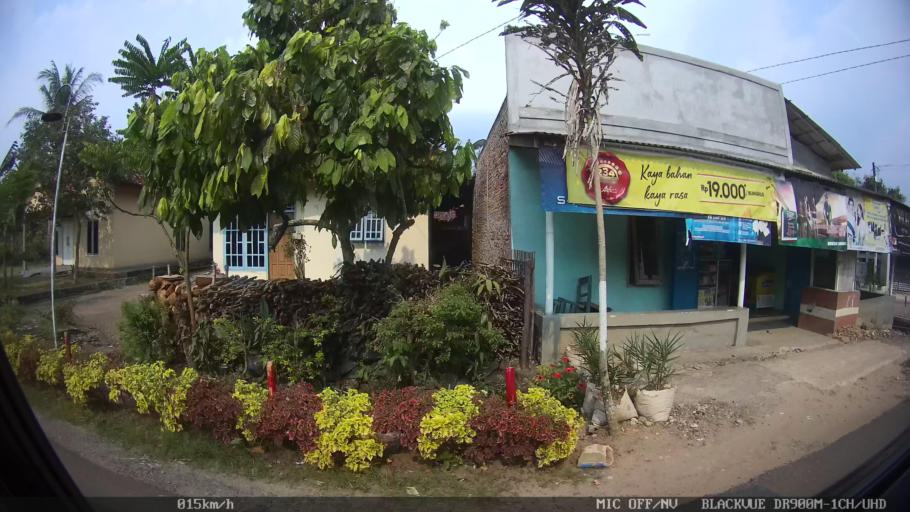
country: ID
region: Lampung
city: Gadingrejo
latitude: -5.4063
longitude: 105.0235
